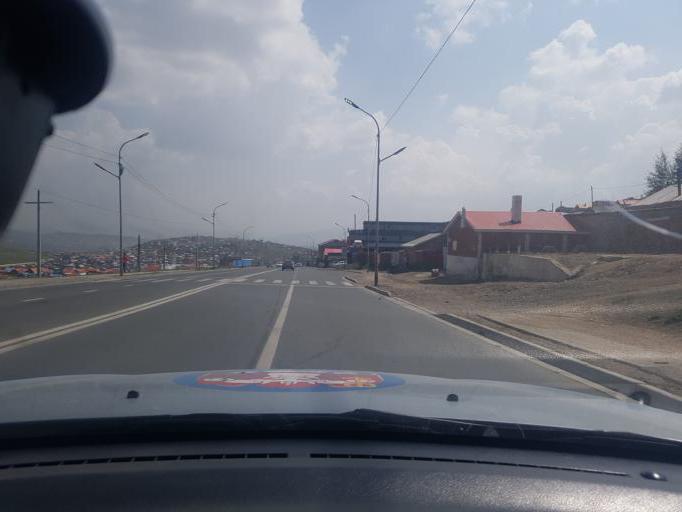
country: MN
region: Ulaanbaatar
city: Ulaanbaatar
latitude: 47.9460
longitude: 106.8690
